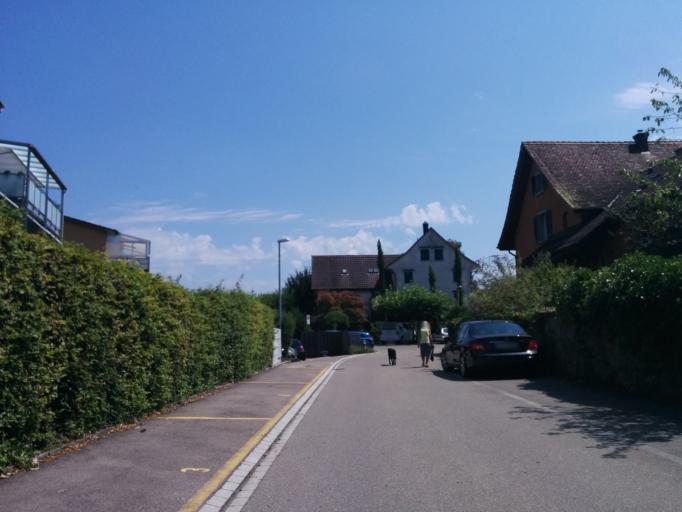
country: CH
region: Zurich
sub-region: Bezirk Meilen
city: Dorf
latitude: 47.2355
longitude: 8.7399
